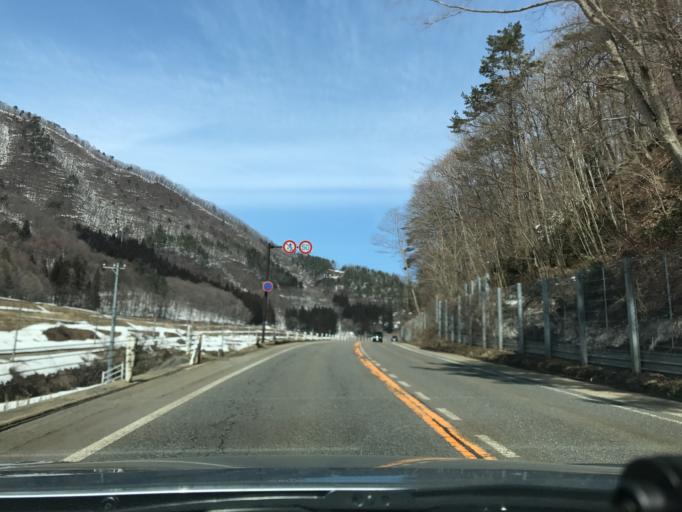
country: JP
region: Nagano
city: Omachi
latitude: 36.5763
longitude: 137.8382
